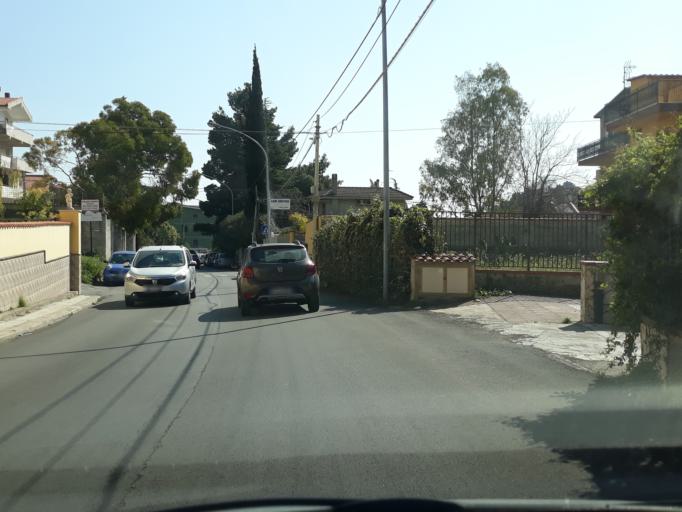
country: IT
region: Sicily
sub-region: Palermo
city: Piano dei Geli
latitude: 38.1174
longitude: 13.2903
